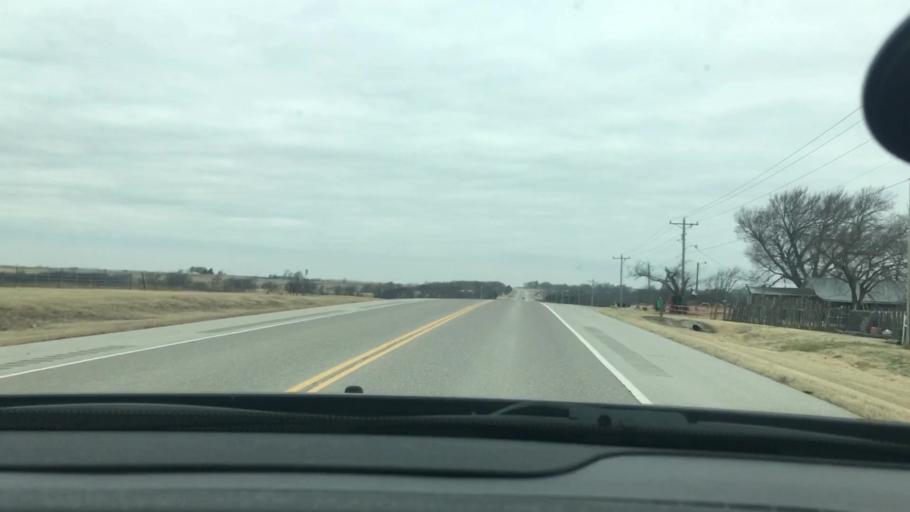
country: US
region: Oklahoma
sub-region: Garvin County
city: Wynnewood
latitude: 34.5135
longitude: -97.3382
